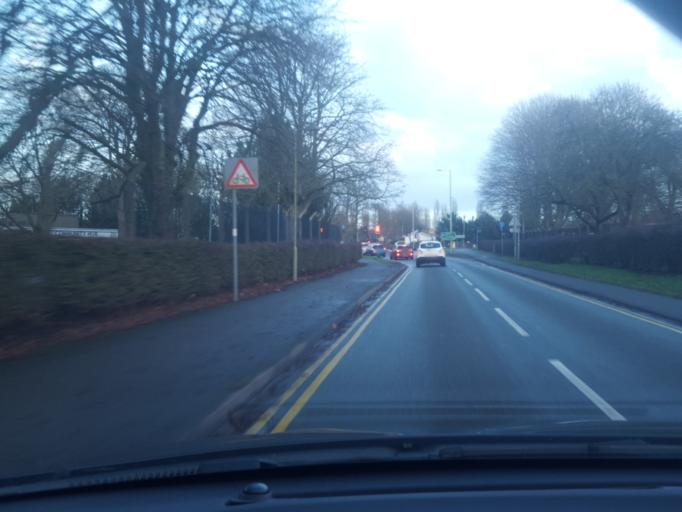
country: GB
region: England
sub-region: Shropshire
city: Tong
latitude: 52.6480
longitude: -2.2949
